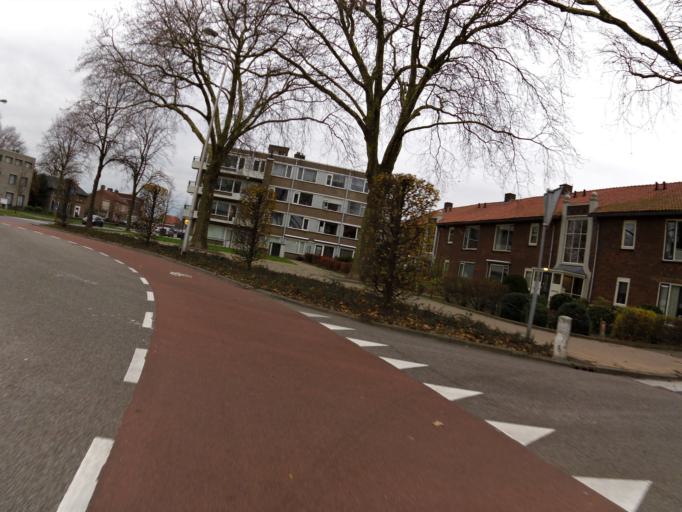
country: NL
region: North Brabant
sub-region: Gemeente Oss
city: Oss
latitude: 51.7577
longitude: 5.5372
